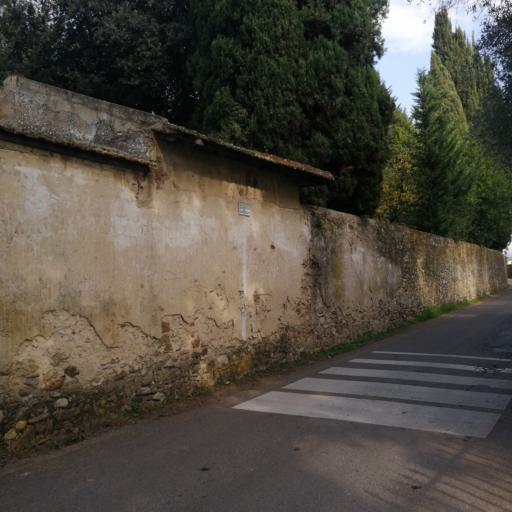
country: IT
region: Tuscany
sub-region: Province of Florence
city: Bagno a Ripoli
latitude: 43.7587
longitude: 11.3181
